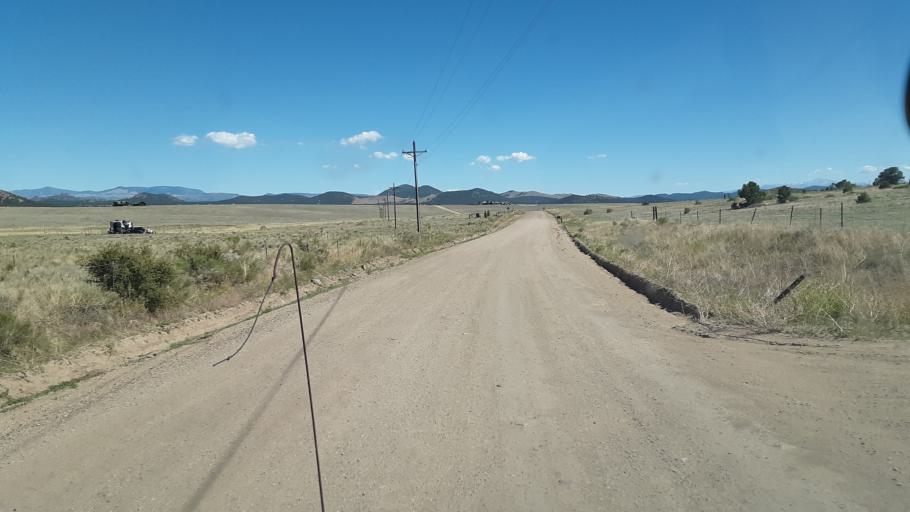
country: US
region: Colorado
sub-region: Custer County
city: Westcliffe
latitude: 38.2476
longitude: -105.5007
